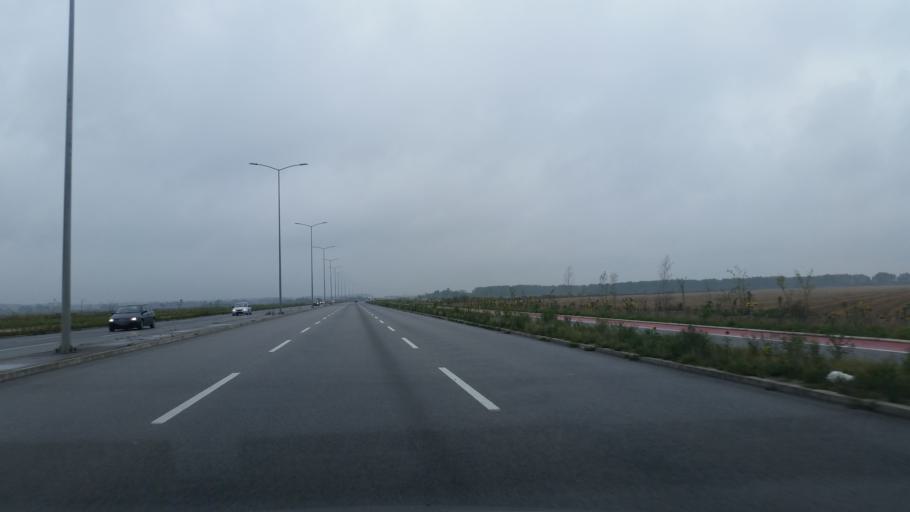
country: RS
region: Central Serbia
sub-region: Belgrade
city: Zemun
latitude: 44.8803
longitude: 20.3955
